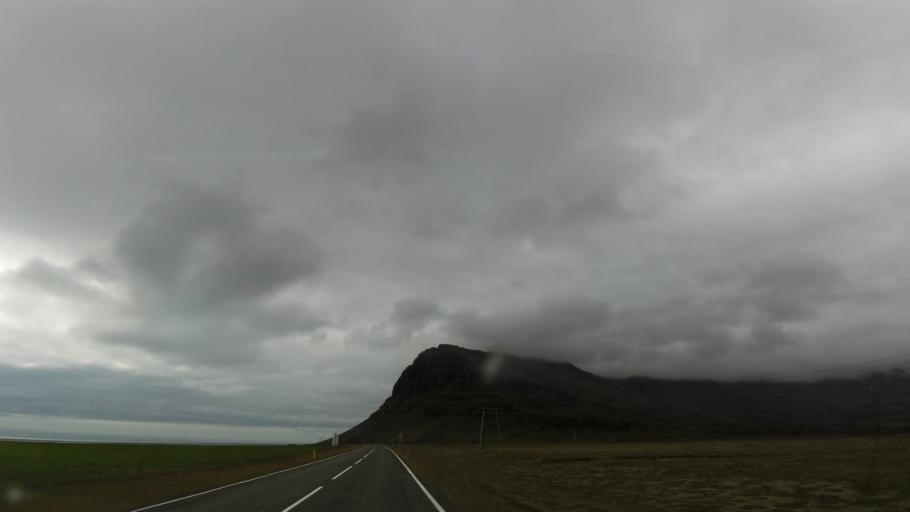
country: IS
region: East
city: Hoefn
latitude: 64.1556
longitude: -15.9443
